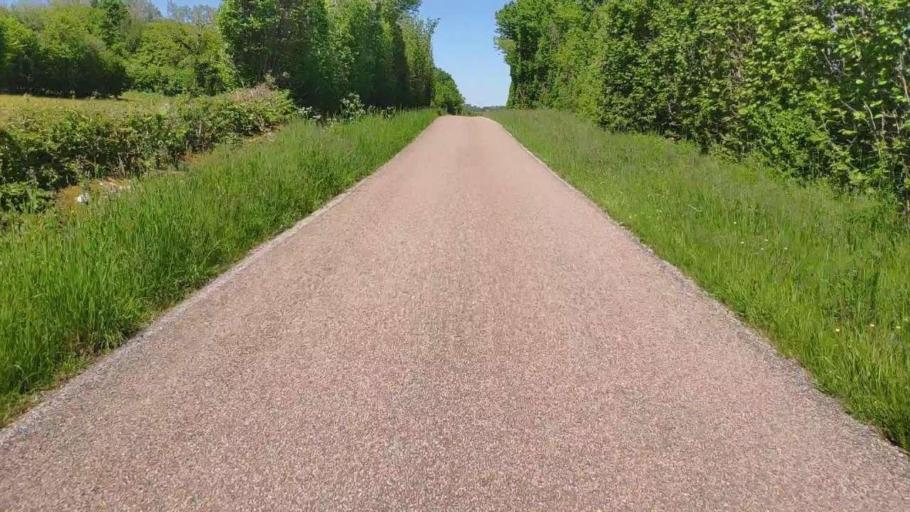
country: FR
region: Franche-Comte
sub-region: Departement du Jura
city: Poligny
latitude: 46.7343
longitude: 5.7215
